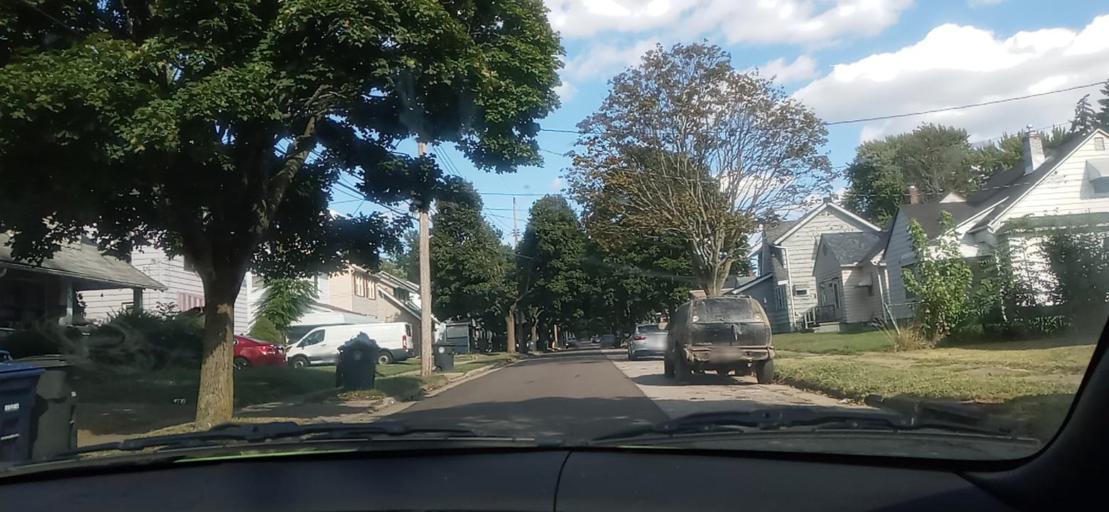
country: US
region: Ohio
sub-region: Summit County
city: Akron
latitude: 41.0545
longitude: -81.5617
